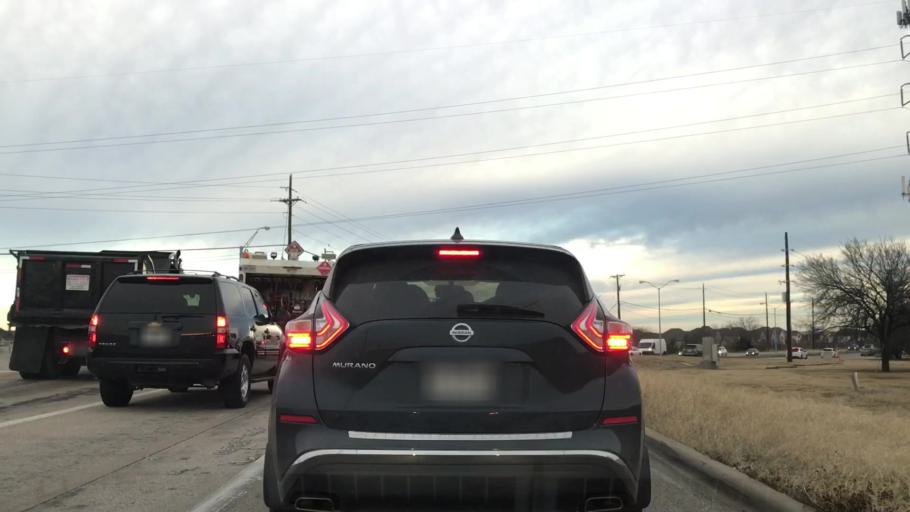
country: US
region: Texas
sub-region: Dallas County
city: Coppell
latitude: 32.9058
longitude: -96.9919
